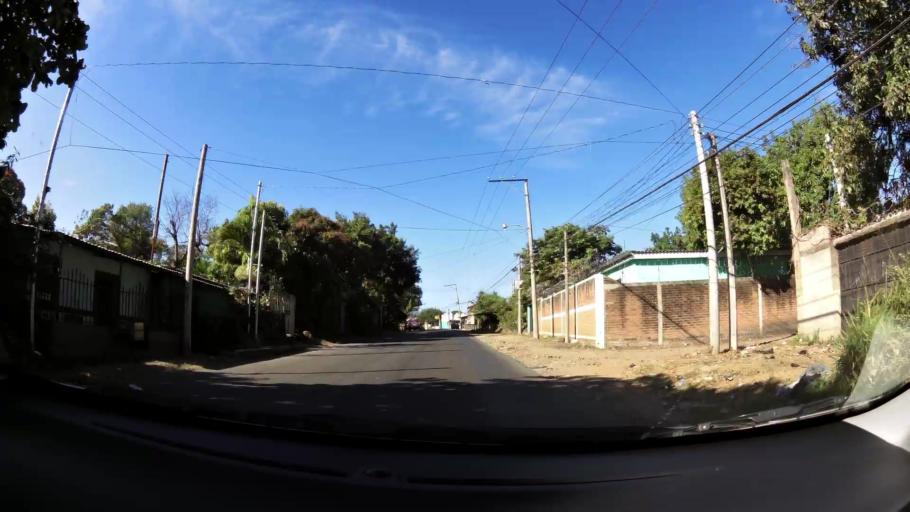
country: SV
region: Santa Ana
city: Santa Ana
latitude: 13.9783
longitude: -89.5796
